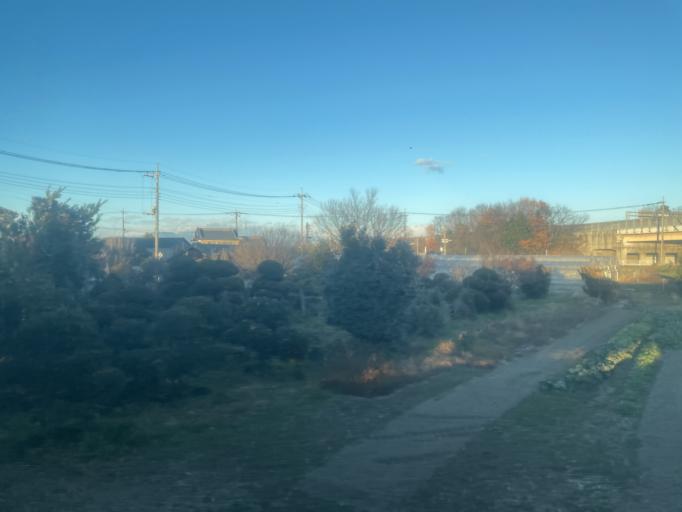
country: JP
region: Gunma
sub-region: Sawa-gun
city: Tamamura
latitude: 36.2781
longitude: 139.0943
